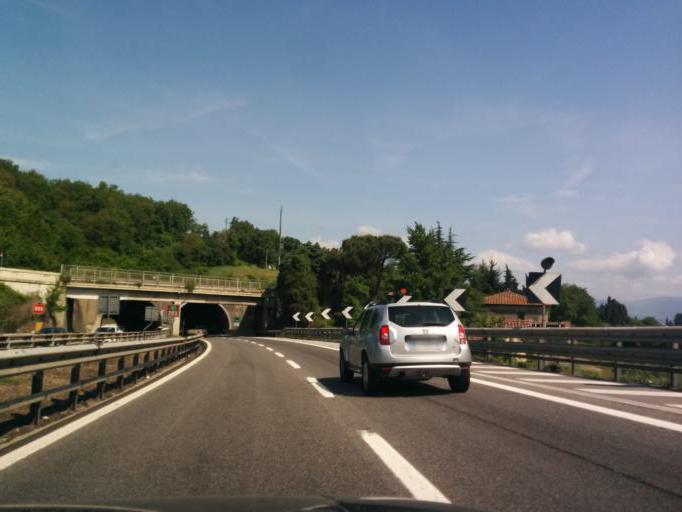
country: IT
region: Tuscany
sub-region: Province of Florence
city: Cavallina
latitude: 43.9514
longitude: 11.2134
